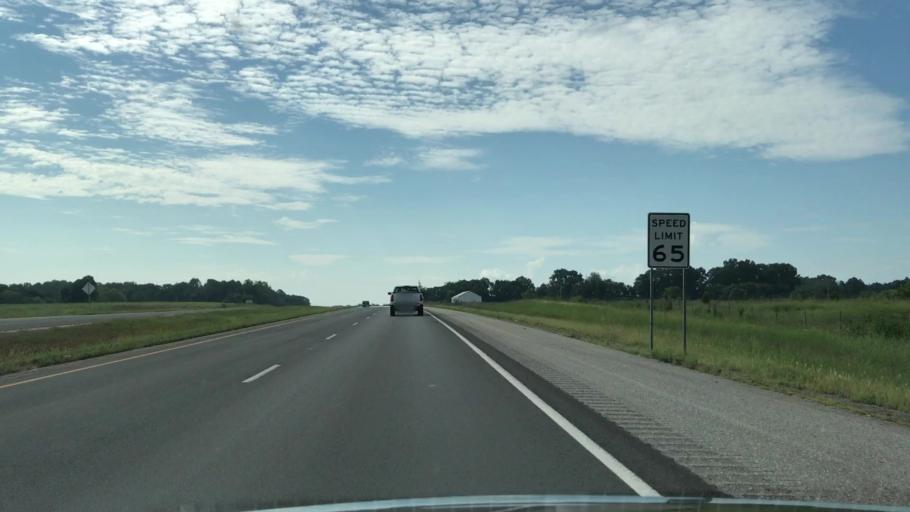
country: US
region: Kentucky
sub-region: Warren County
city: Plano
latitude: 36.8227
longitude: -86.3101
